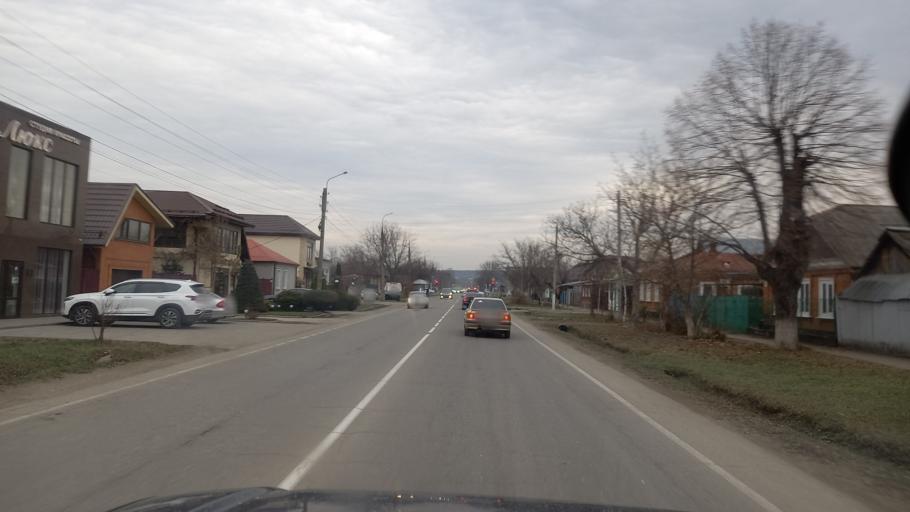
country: RU
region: Adygeya
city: Maykop
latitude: 44.5993
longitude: 40.1217
